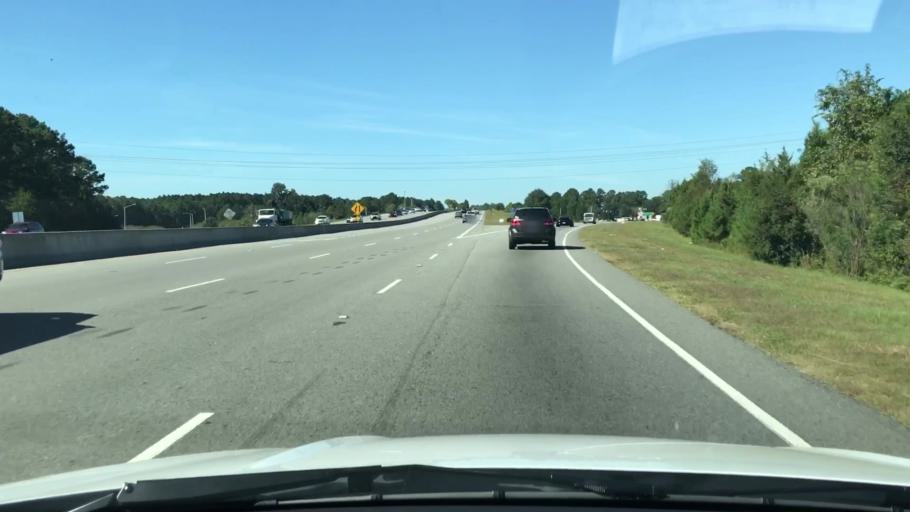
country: US
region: South Carolina
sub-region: Beaufort County
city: Bluffton
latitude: 32.2912
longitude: -80.9332
